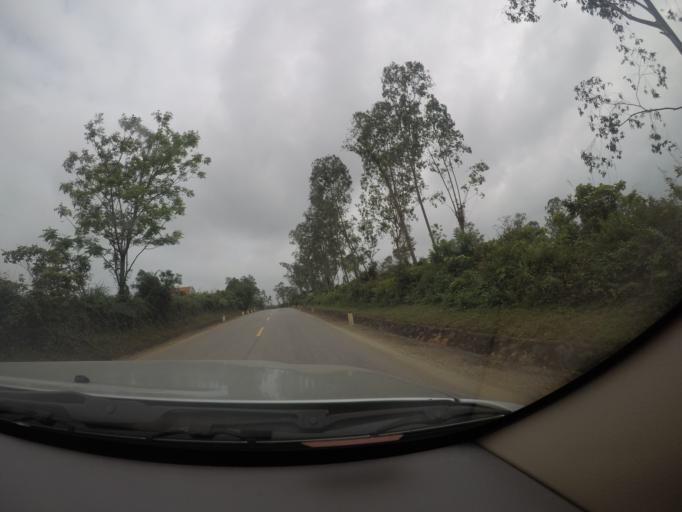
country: VN
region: Quang Binh
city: Hoan Lao
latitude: 17.4941
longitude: 106.5117
